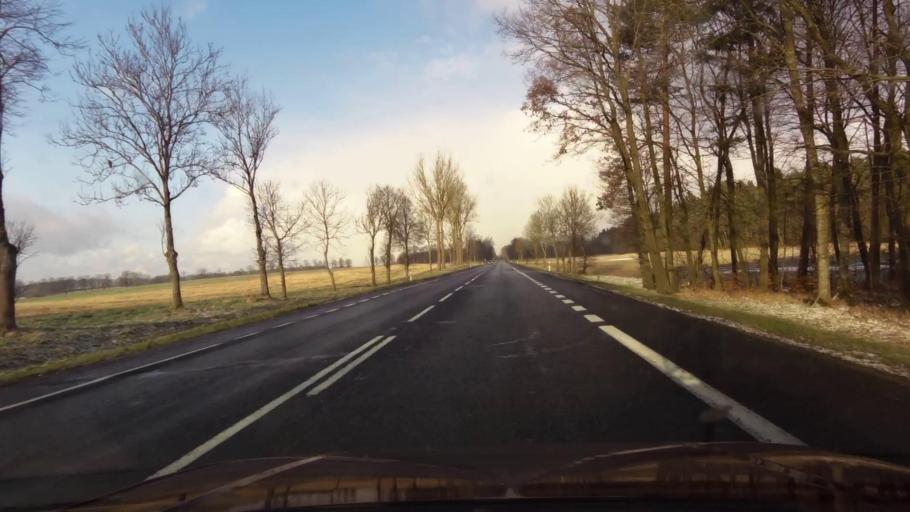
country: PL
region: West Pomeranian Voivodeship
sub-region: Powiat bialogardzki
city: Bialogard
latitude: 54.0933
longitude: 15.9917
